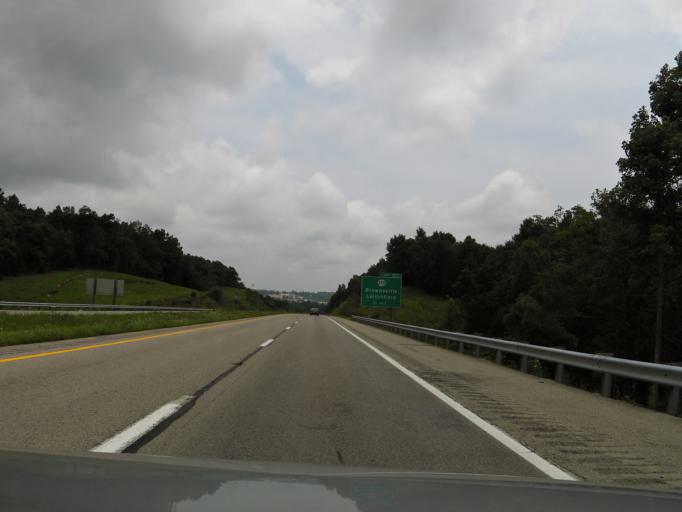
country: US
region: Kentucky
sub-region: Grayson County
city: Leitchfield
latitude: 37.4608
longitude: -86.3065
